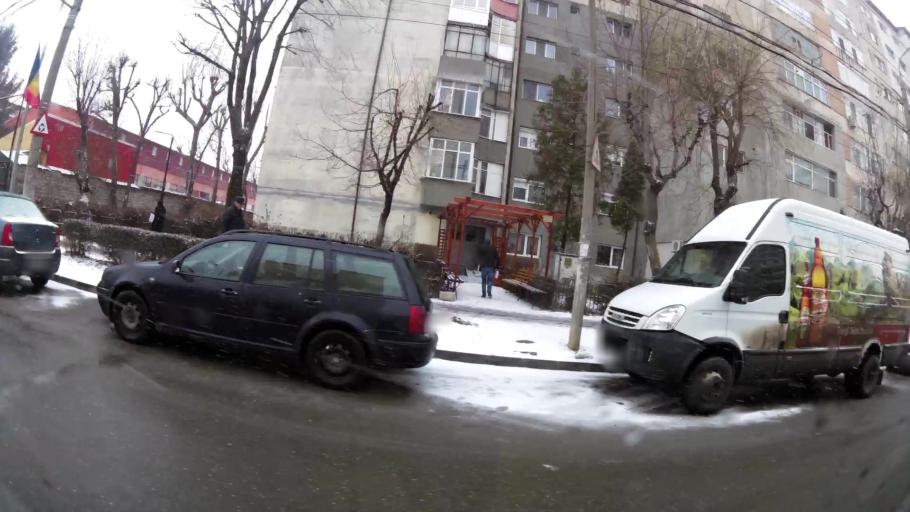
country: RO
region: Dambovita
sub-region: Municipiul Targoviste
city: Targoviste
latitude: 44.9205
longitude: 25.4497
